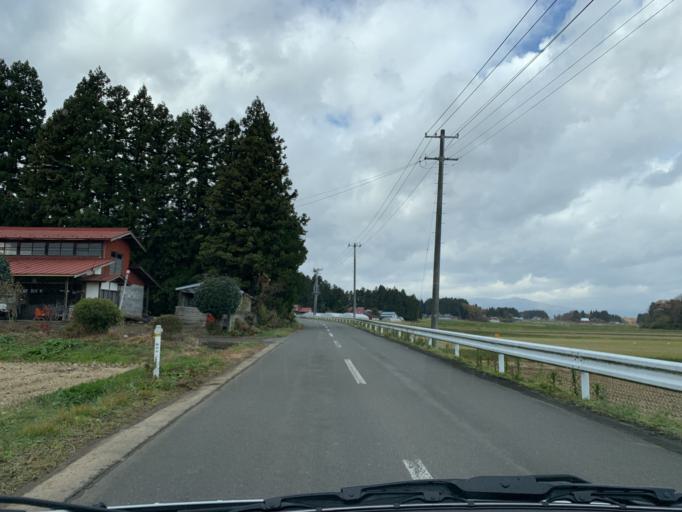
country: JP
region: Iwate
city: Mizusawa
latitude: 39.0712
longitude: 141.0698
